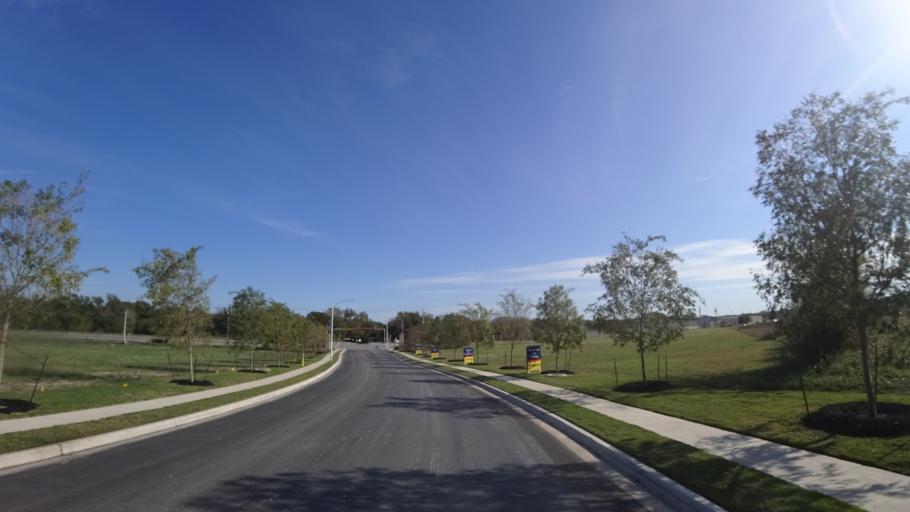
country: US
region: Texas
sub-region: Travis County
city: Pflugerville
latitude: 30.4077
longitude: -97.6372
